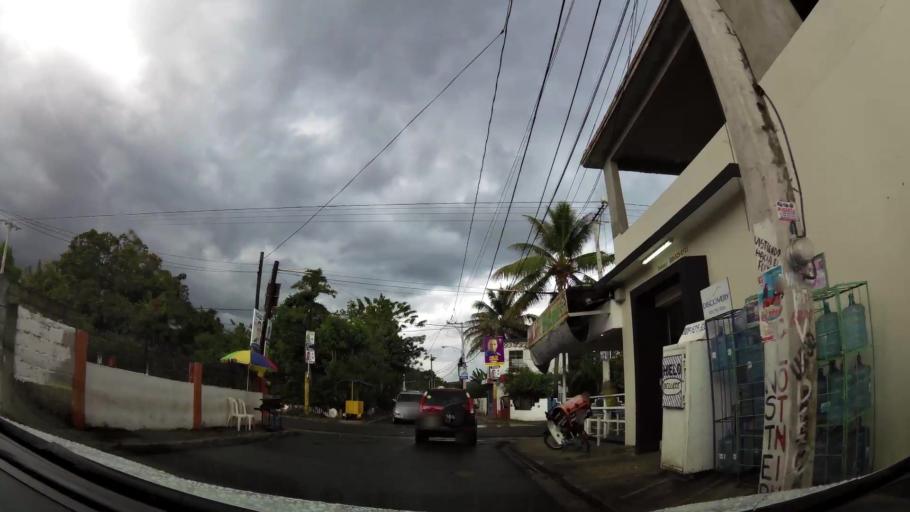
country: DO
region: Monsenor Nouel
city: Bonao
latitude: 18.9361
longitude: -70.3990
